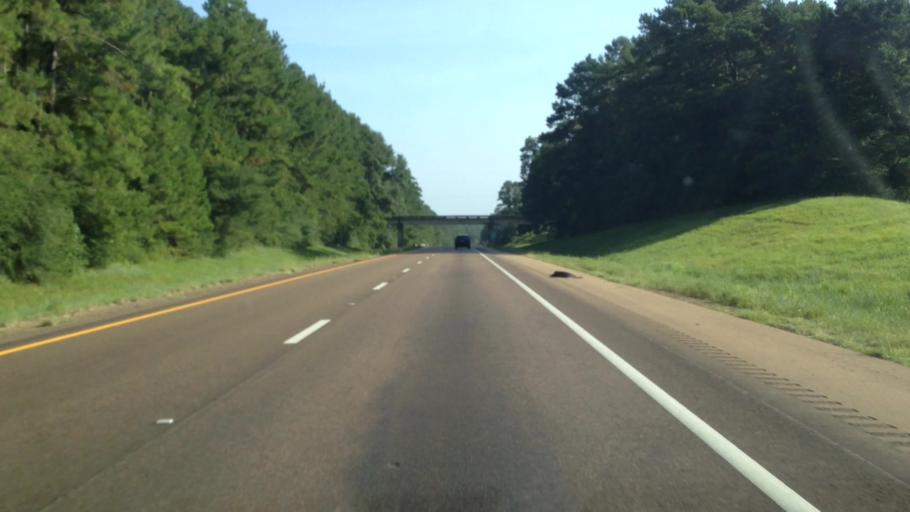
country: US
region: Mississippi
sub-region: Pike County
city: Summit
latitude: 31.3472
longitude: -90.4784
